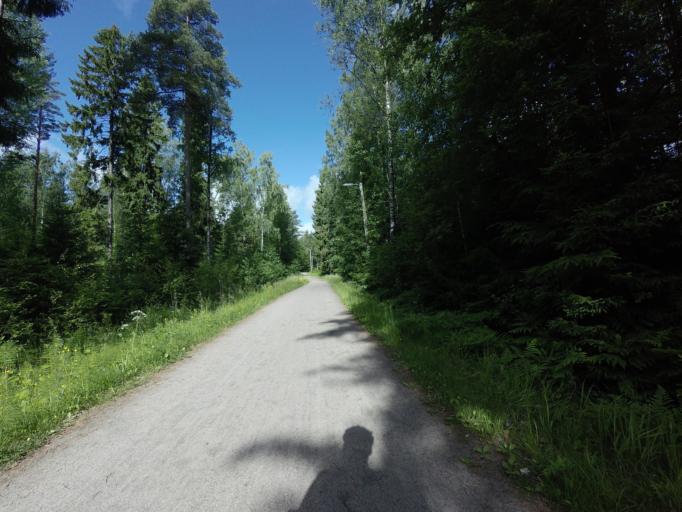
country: FI
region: Uusimaa
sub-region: Helsinki
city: Espoo
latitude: 60.1842
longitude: 24.6410
